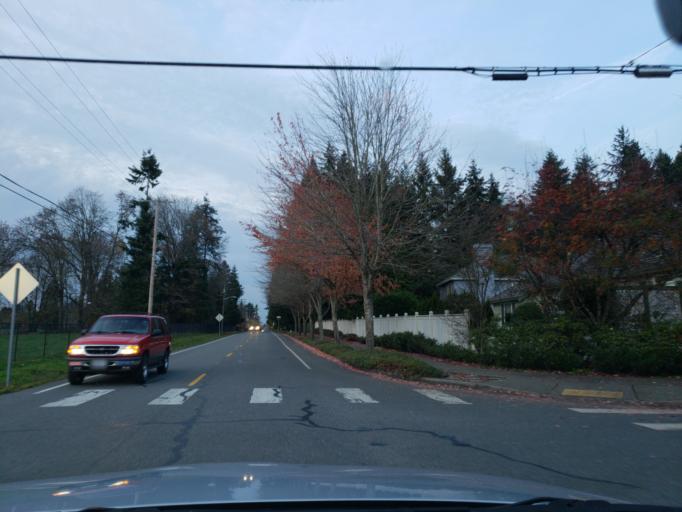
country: US
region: Washington
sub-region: King County
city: Bothell
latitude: 47.7658
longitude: -122.2232
